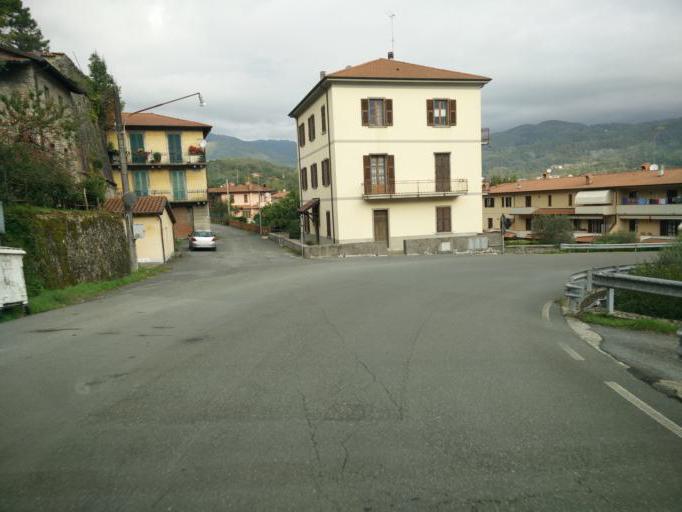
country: IT
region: Tuscany
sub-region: Provincia di Massa-Carrara
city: Pontremoli
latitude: 44.3741
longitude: 9.8733
